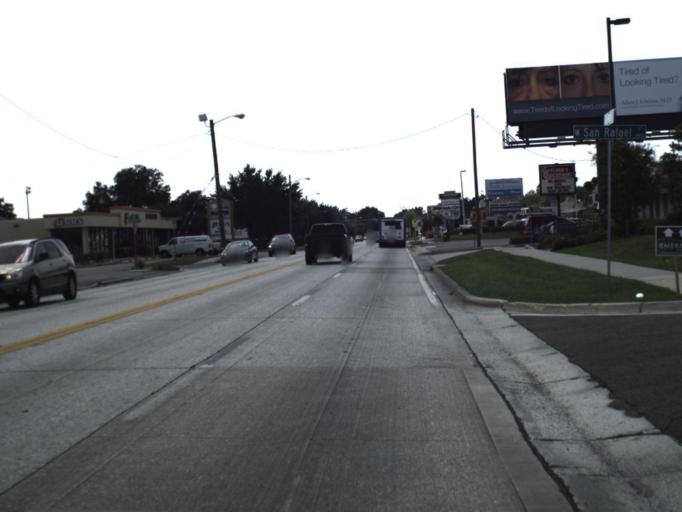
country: US
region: Florida
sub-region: Hillsborough County
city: Tampa
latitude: 27.9267
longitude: -82.5059
